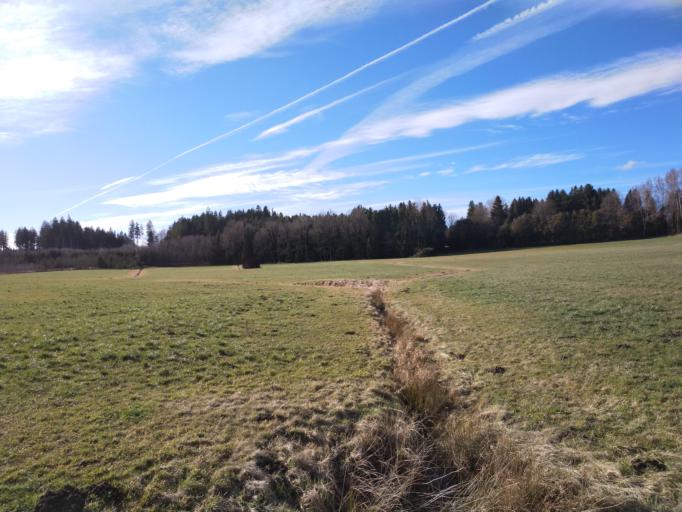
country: DE
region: Bavaria
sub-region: Swabia
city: Bad Worishofen
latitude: 47.9946
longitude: 10.5803
